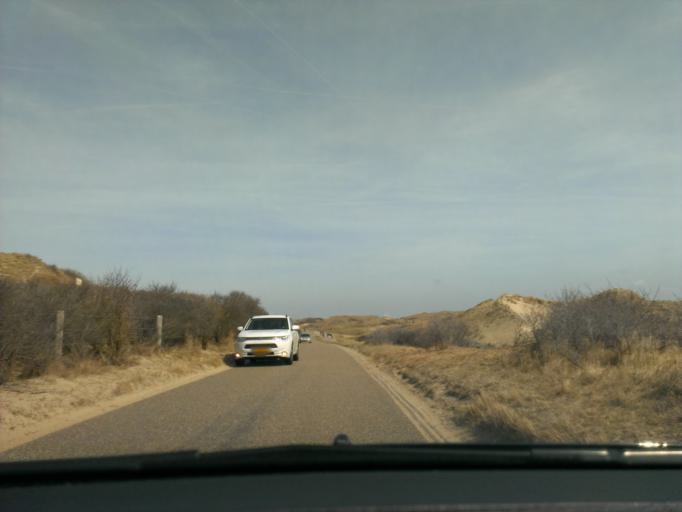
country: NL
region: North Holland
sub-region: Gemeente Zandvoort
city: Zandvoort
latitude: 52.4114
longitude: 4.5507
